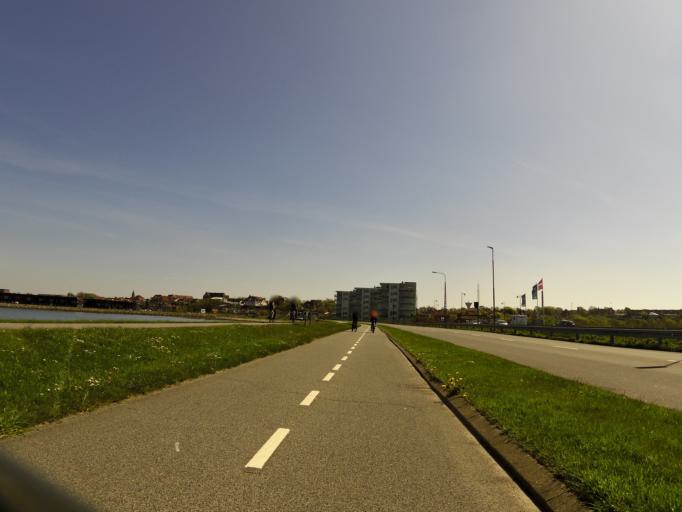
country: DK
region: Central Jutland
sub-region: Struer Kommune
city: Struer
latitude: 56.4973
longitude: 8.5831
